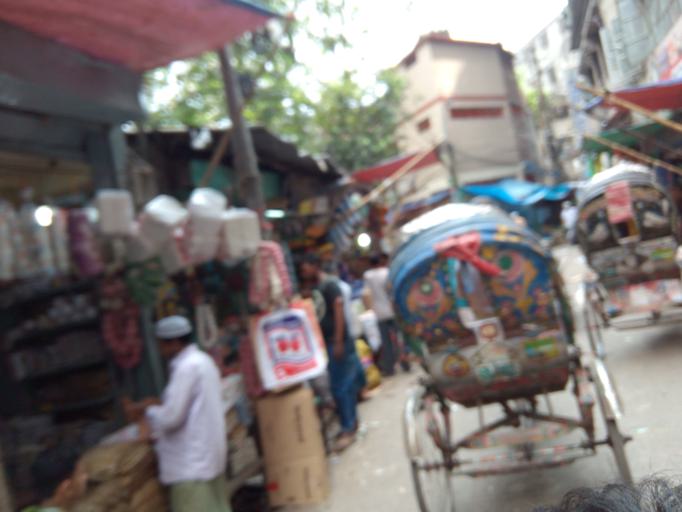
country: BD
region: Dhaka
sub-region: Dhaka
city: Dhaka
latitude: 23.7213
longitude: 90.4138
